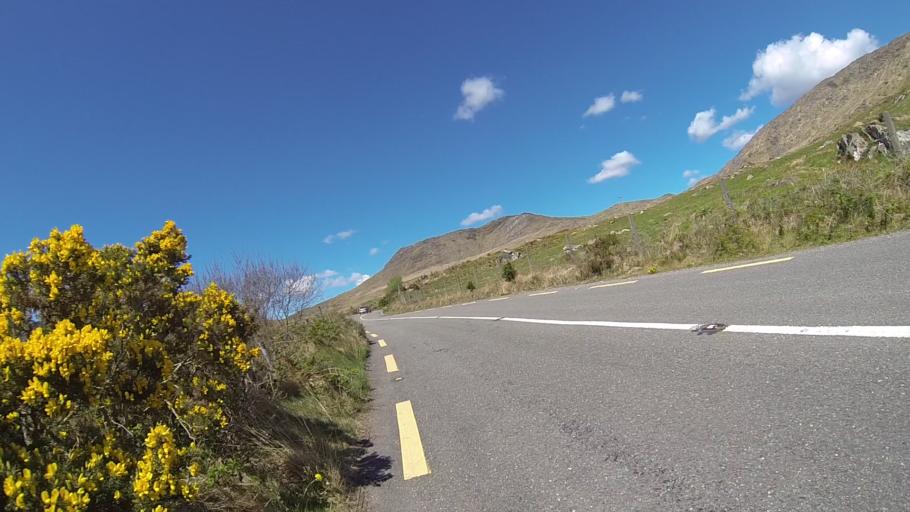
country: IE
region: Munster
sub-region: Ciarrai
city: Kenmare
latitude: 51.9229
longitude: -9.6304
